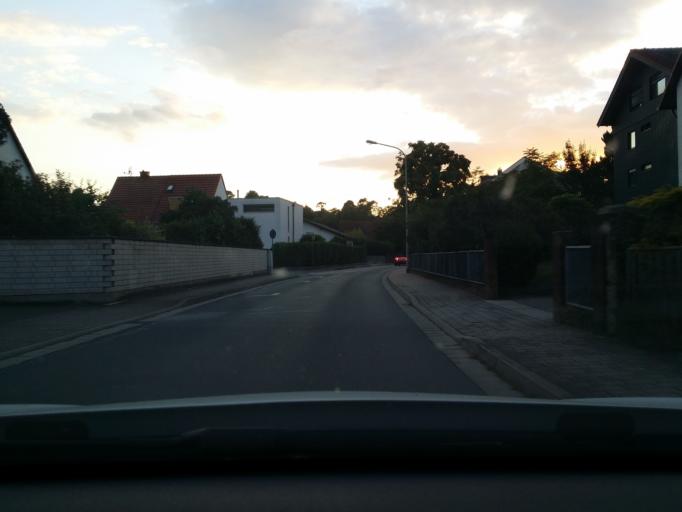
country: DE
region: Hesse
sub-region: Regierungsbezirk Darmstadt
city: Seeheim-Jugenheim
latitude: 49.7742
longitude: 8.6335
